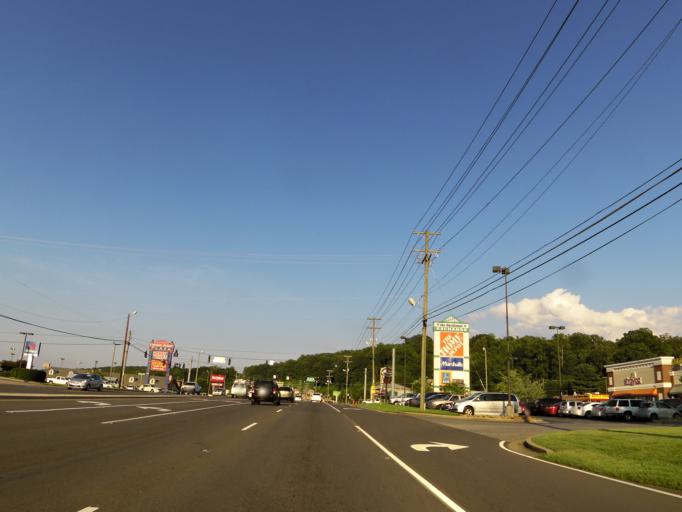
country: US
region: Tennessee
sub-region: Knox County
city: Knoxville
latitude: 36.0068
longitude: -84.0210
